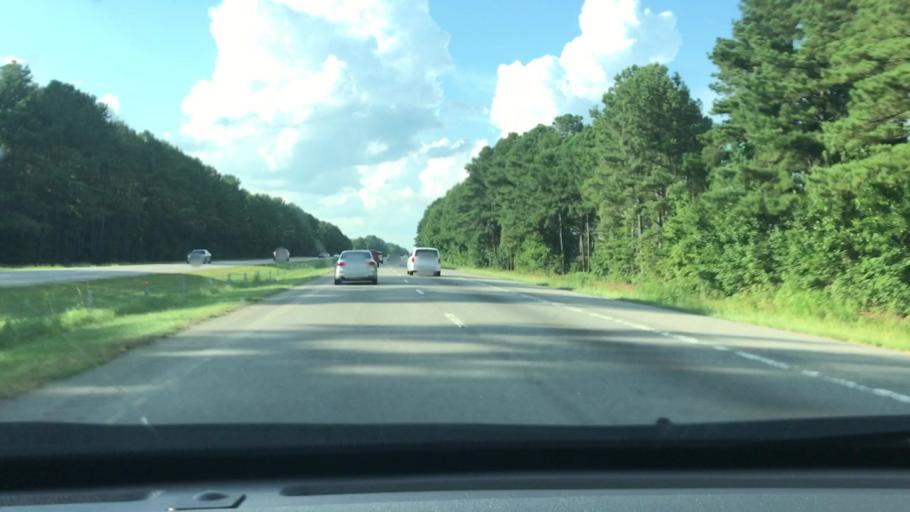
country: US
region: North Carolina
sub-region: Robeson County
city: Saint Pauls
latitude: 34.7576
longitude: -78.9969
